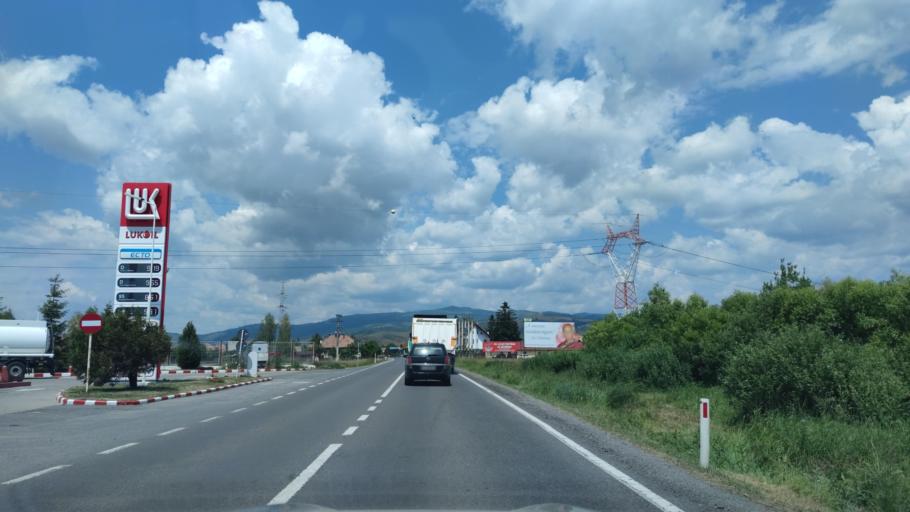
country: RO
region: Harghita
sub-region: Municipiul Gheorgheni
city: Gheorgheni
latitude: 46.7120
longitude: 25.6024
